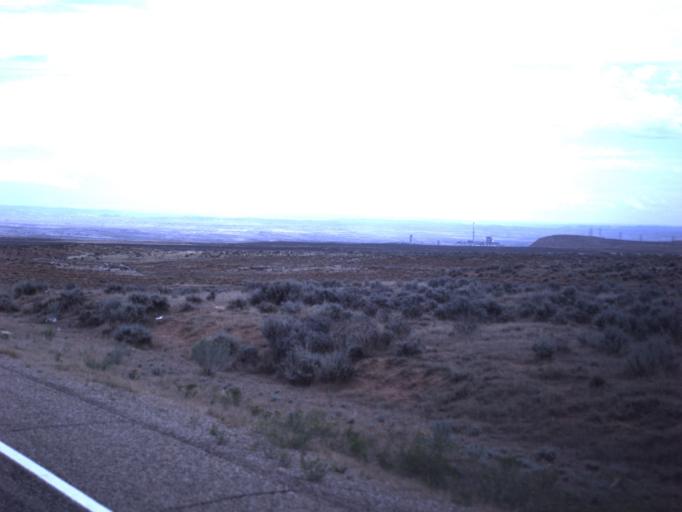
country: US
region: Utah
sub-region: Uintah County
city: Naples
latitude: 40.1515
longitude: -109.3005
